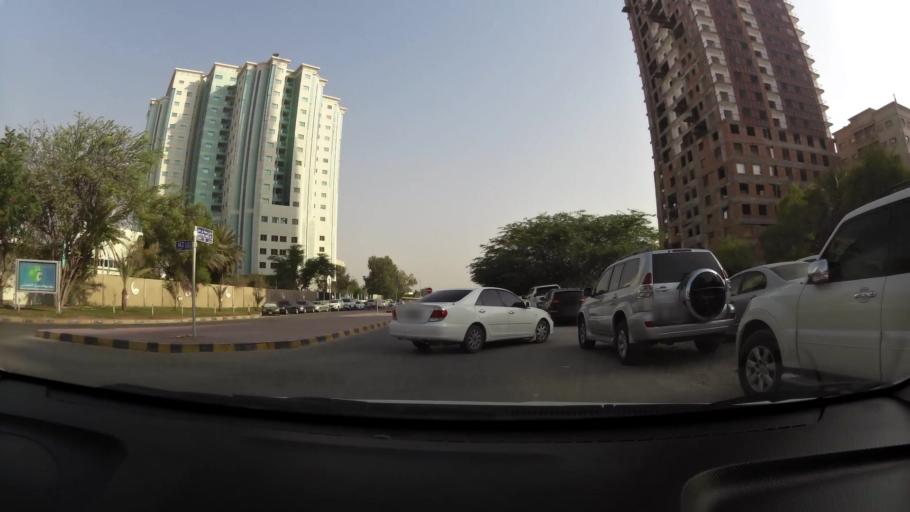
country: AE
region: Ajman
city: Ajman
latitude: 25.3904
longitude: 55.4368
